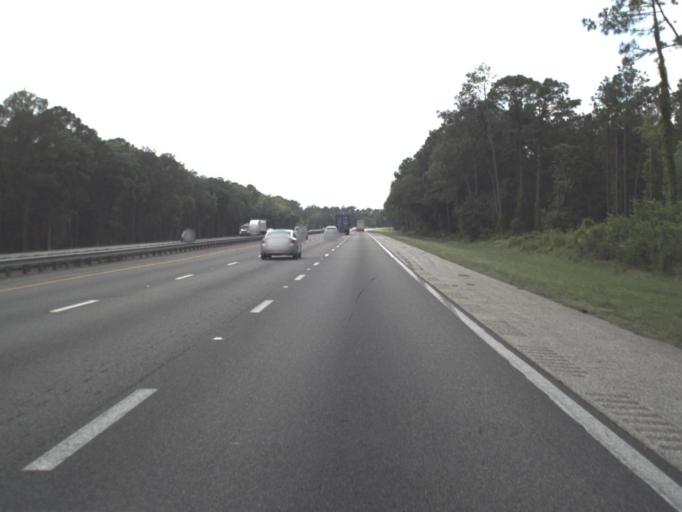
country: US
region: Florida
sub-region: Saint Johns County
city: Butler Beach
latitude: 29.6743
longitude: -81.3084
